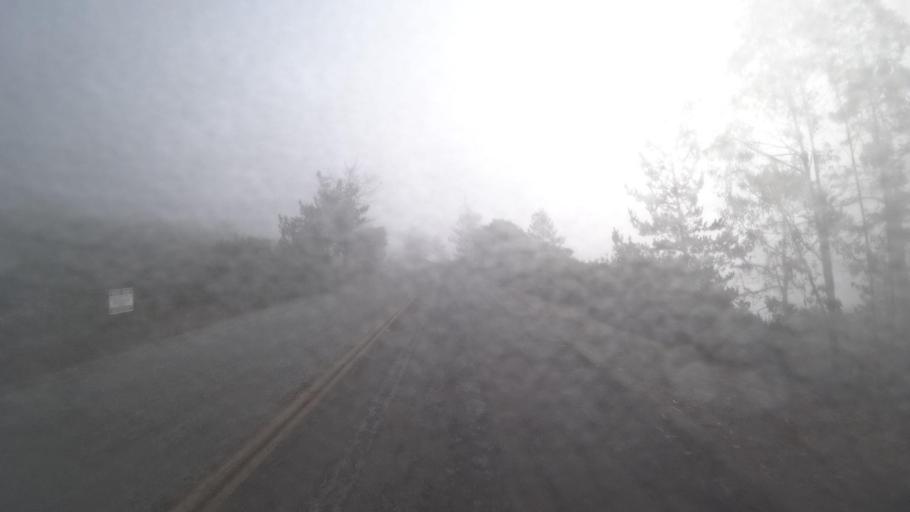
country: US
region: California
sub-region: Monterey County
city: Del Rey Oaks
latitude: 36.5790
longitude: -121.7918
